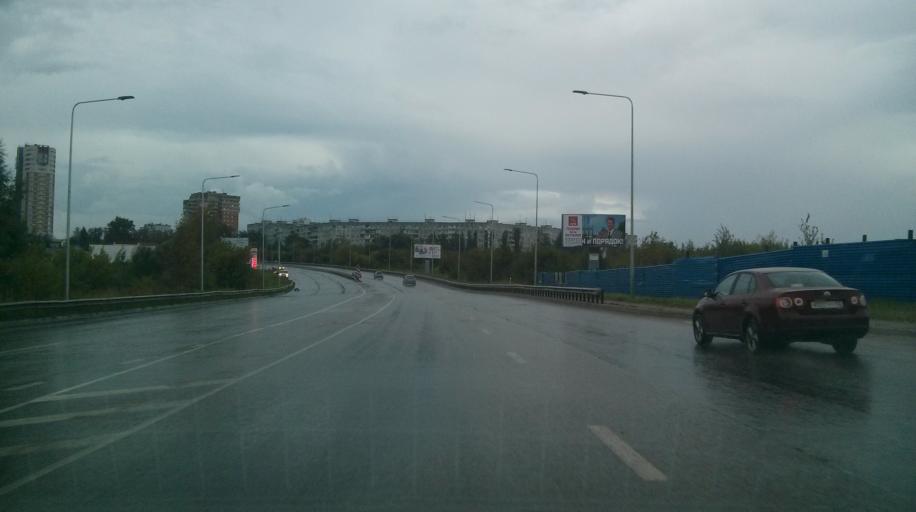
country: RU
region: Nizjnij Novgorod
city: Nizhniy Novgorod
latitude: 56.2772
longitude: 44.0335
